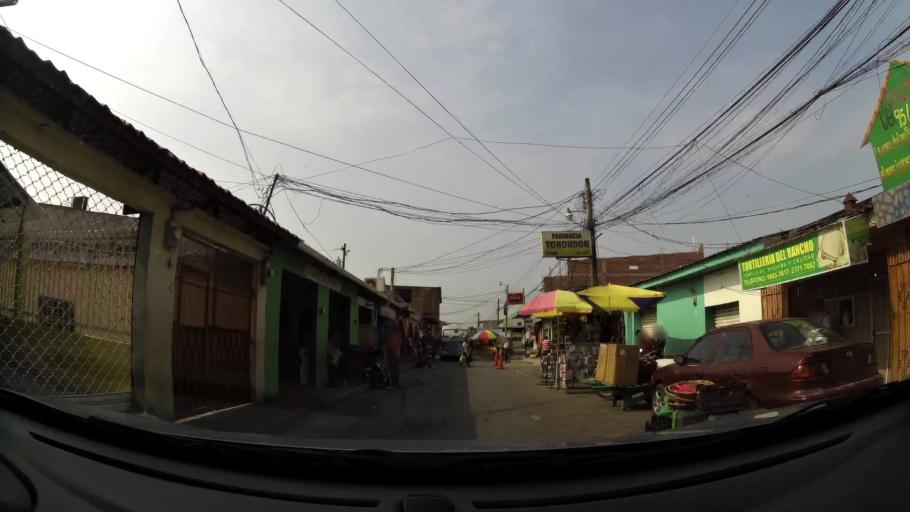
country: HN
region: Comayagua
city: Comayagua
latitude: 14.4545
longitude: -87.6413
